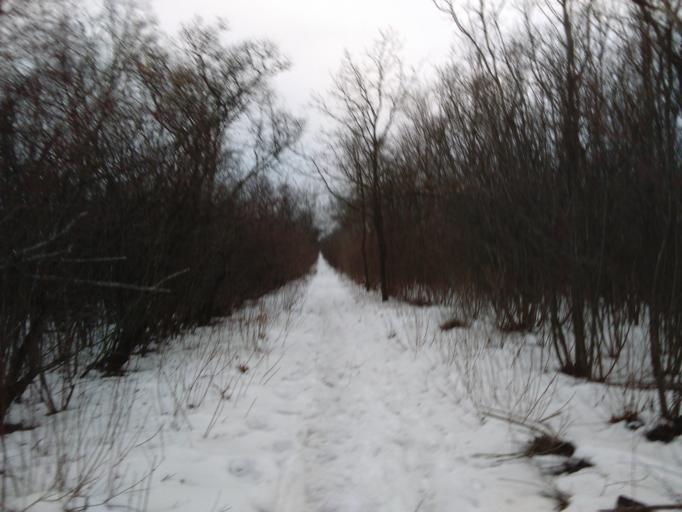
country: RU
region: Rostov
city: Temernik
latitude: 47.3531
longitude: 39.7398
